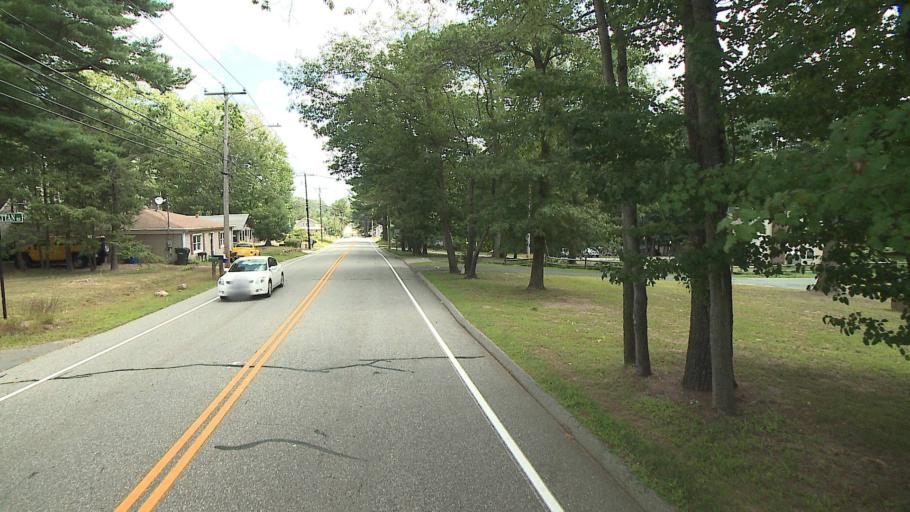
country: US
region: Connecticut
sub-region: Tolland County
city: Crystal Lake
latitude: 41.9316
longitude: -72.3772
